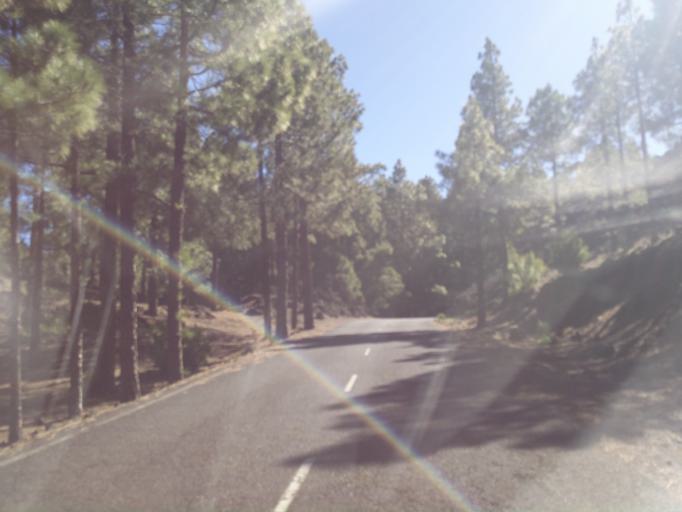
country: ES
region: Canary Islands
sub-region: Provincia de Santa Cruz de Tenerife
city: El Paso
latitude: 28.6158
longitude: -17.8442
